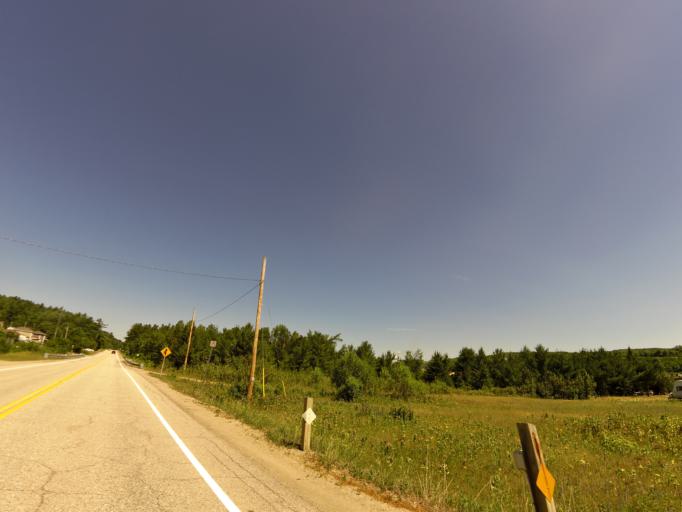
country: CA
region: Quebec
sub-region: Abitibi-Temiscamingue
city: Temiscaming
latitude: 46.6988
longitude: -79.0997
